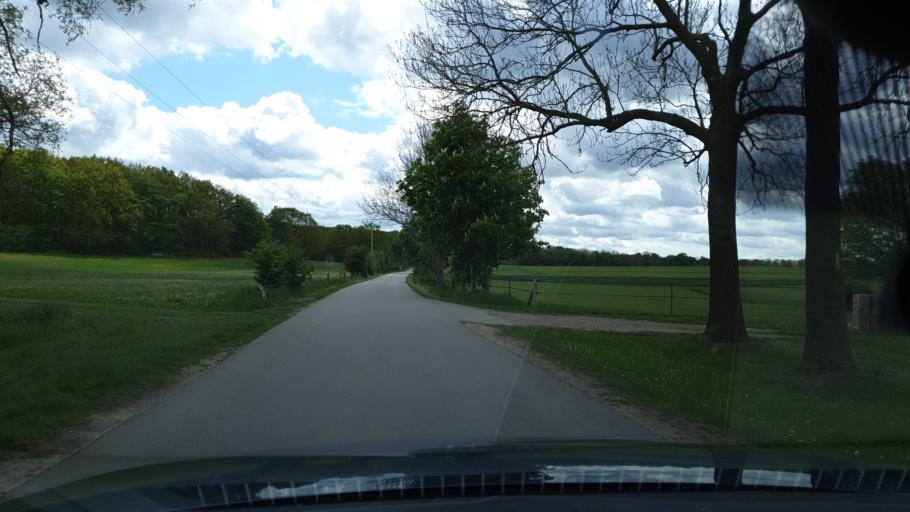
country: DE
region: Mecklenburg-Vorpommern
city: Jurgenshagen
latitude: 53.9404
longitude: 11.8820
